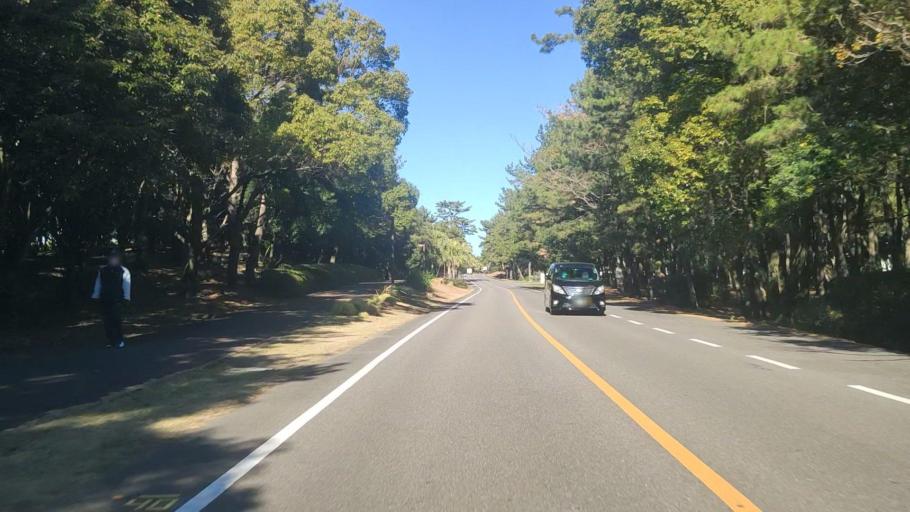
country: JP
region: Miyazaki
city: Miyazaki-shi
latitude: 31.9502
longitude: 131.4662
